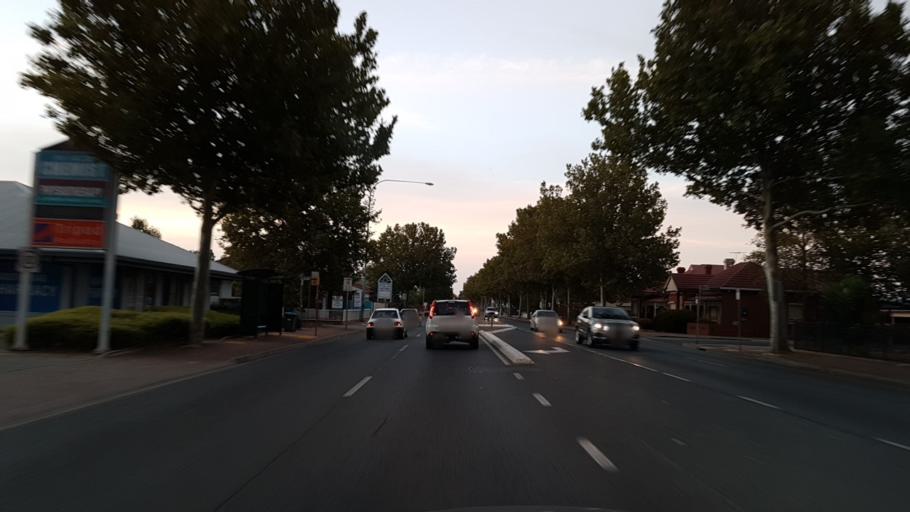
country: AU
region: South Australia
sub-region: City of West Torrens
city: Thebarton
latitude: -34.9290
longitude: 138.5700
